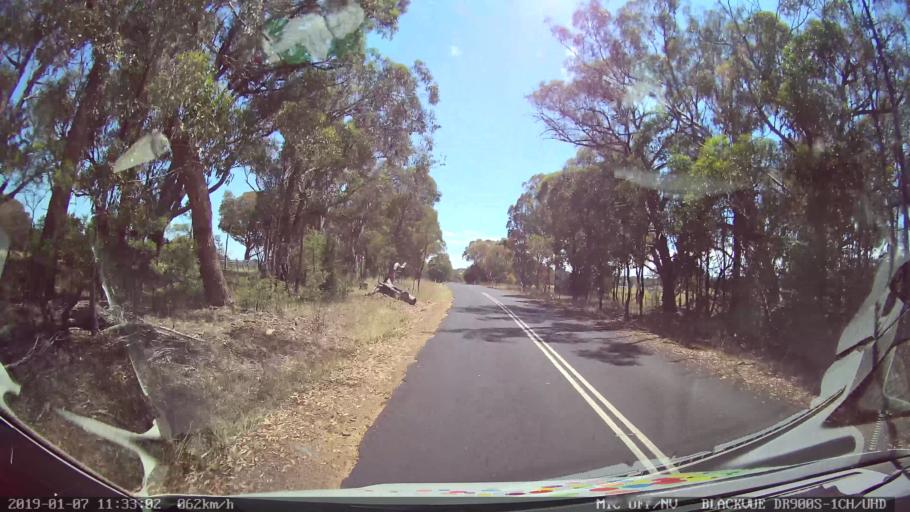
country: AU
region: New South Wales
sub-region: Armidale Dumaresq
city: Armidale
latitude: -30.4040
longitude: 151.5600
